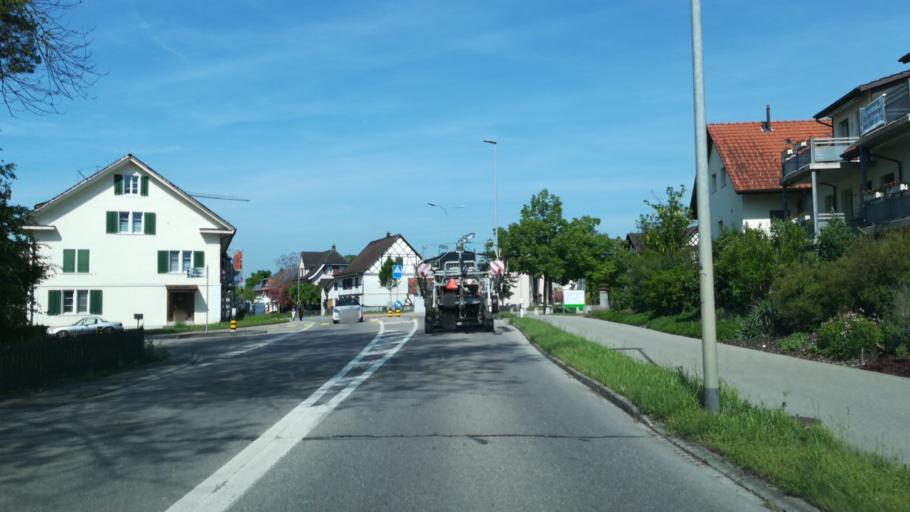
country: CH
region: Thurgau
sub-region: Frauenfeld District
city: Pfyn
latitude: 47.5965
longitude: 8.9588
